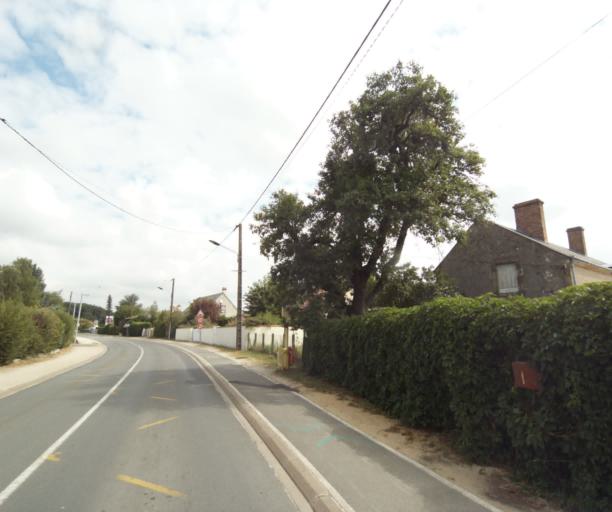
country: FR
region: Centre
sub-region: Departement du Loiret
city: Checy
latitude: 47.9011
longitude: 2.0278
